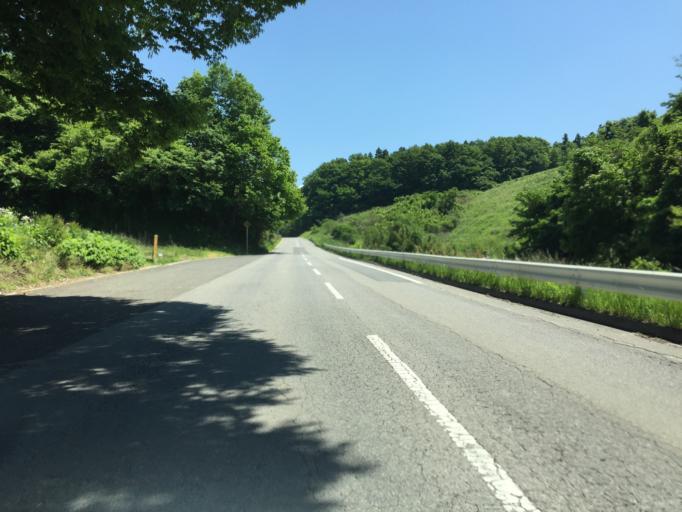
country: JP
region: Fukushima
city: Miharu
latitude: 37.4978
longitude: 140.4913
